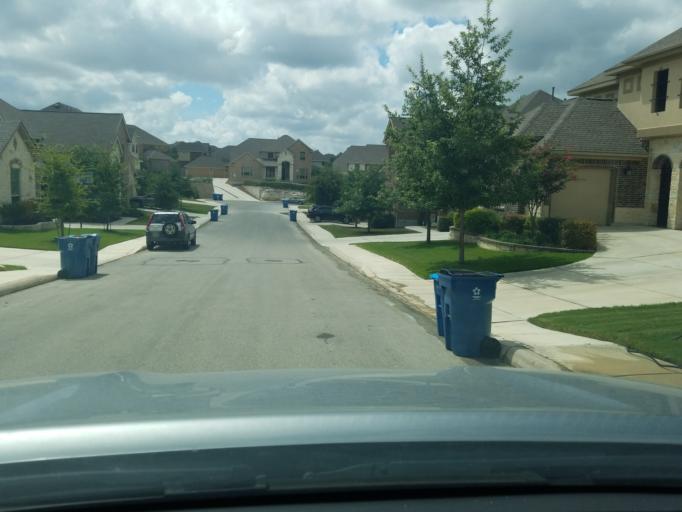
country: US
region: Texas
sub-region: Bexar County
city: Timberwood Park
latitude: 29.6685
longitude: -98.5077
